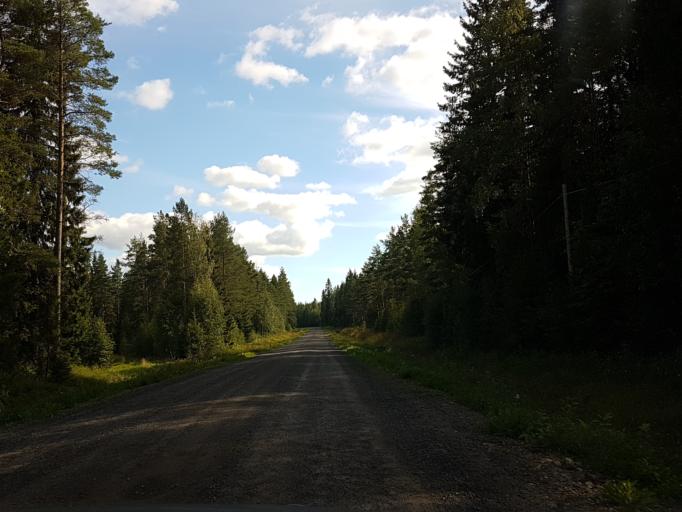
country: SE
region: Vaesterbotten
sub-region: Robertsfors Kommun
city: Robertsfors
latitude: 64.1737
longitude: 20.6458
